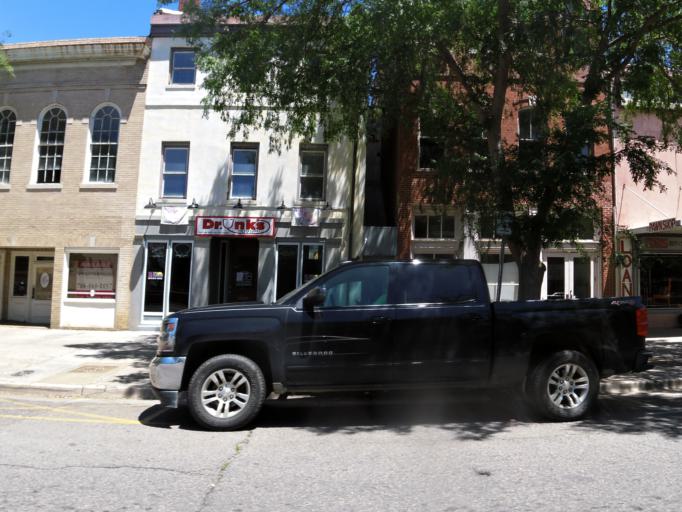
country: US
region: Georgia
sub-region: Richmond County
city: Augusta
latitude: 33.4760
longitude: -81.9671
